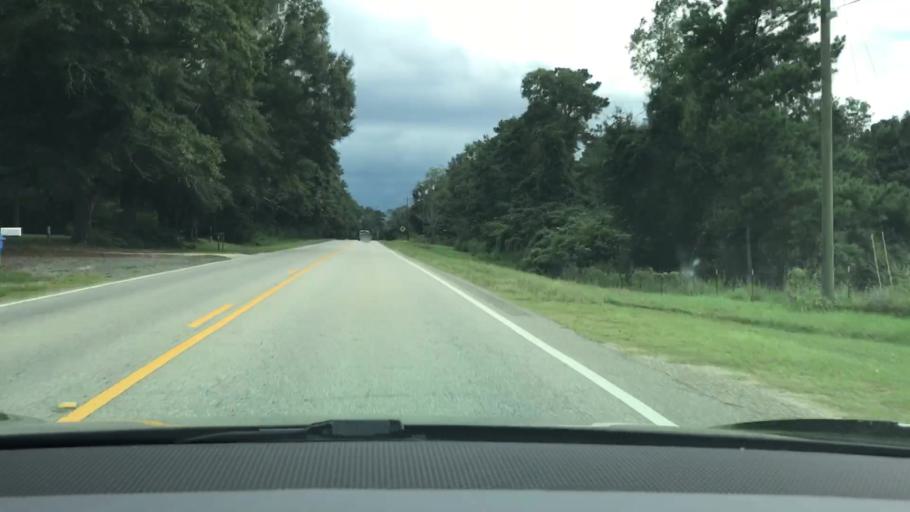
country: US
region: Alabama
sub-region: Coffee County
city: Elba
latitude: 31.5276
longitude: -86.0355
